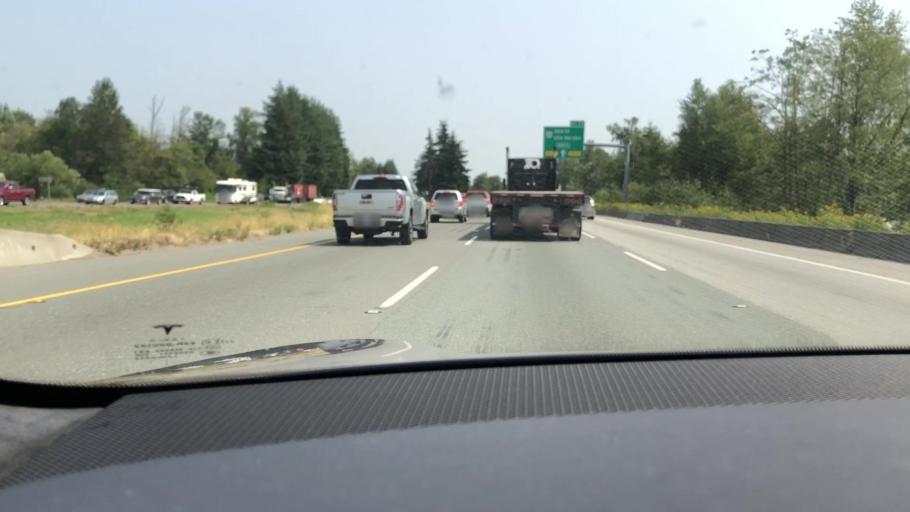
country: CA
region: British Columbia
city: Aldergrove
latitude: 49.1058
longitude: -122.5041
